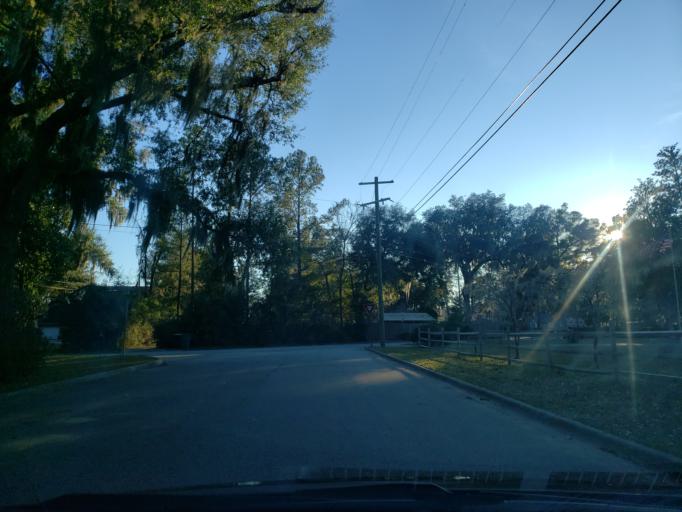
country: US
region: Georgia
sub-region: Chatham County
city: Montgomery
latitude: 31.9886
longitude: -81.1144
